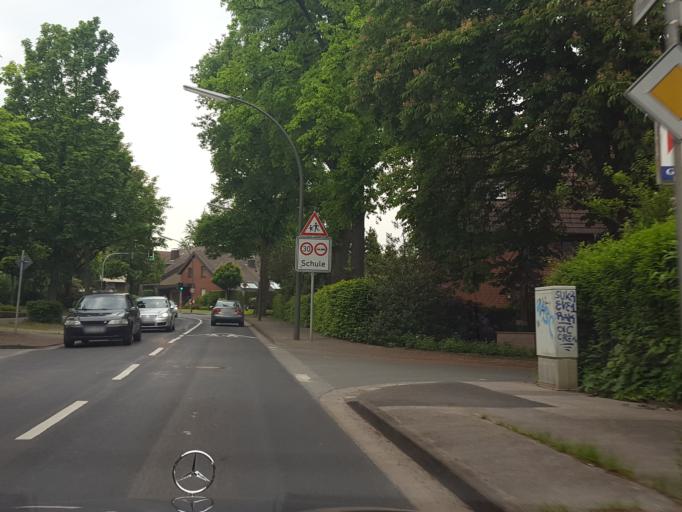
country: DE
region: North Rhine-Westphalia
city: Oer-Erkenschwick
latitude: 51.6237
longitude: 7.2509
